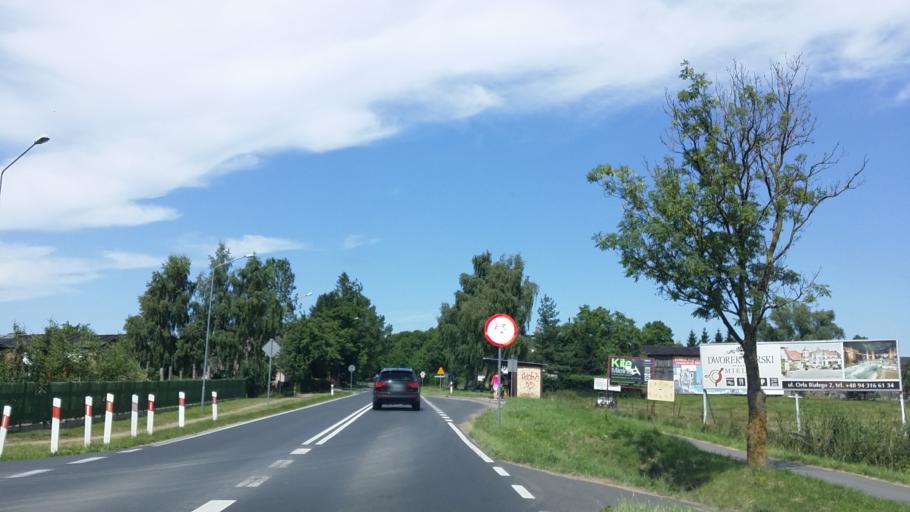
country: PL
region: West Pomeranian Voivodeship
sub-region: Powiat koszalinski
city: Mielno
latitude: 54.2380
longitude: 16.0708
